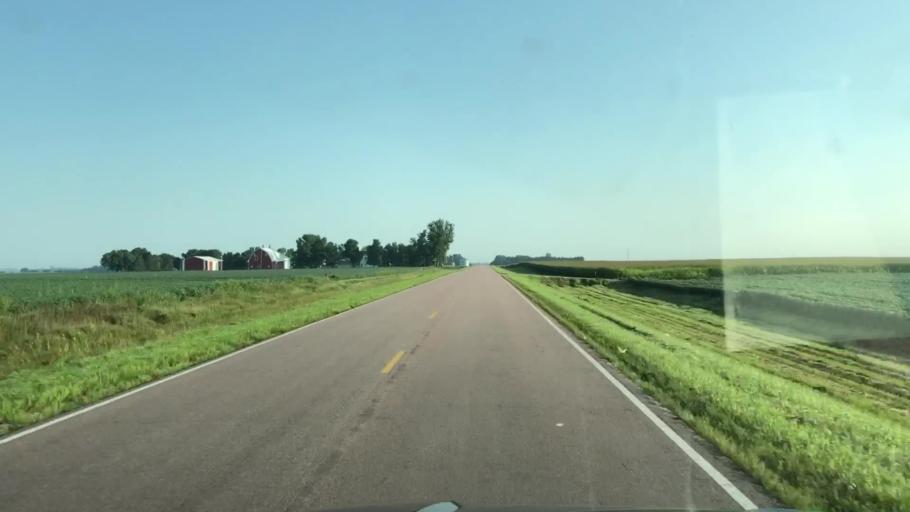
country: US
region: Iowa
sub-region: Lyon County
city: George
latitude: 43.3081
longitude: -95.9992
